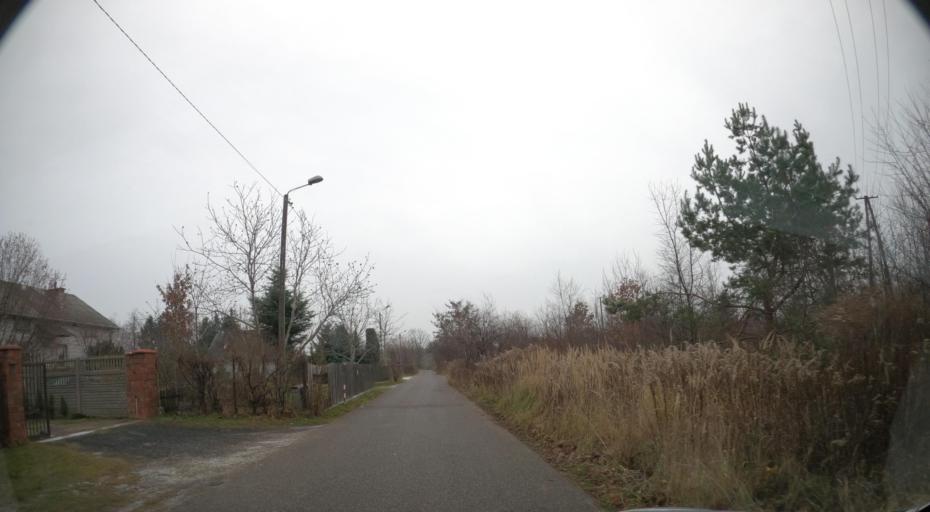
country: PL
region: Masovian Voivodeship
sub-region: Powiat radomski
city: Jastrzebia
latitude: 51.4309
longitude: 21.2302
